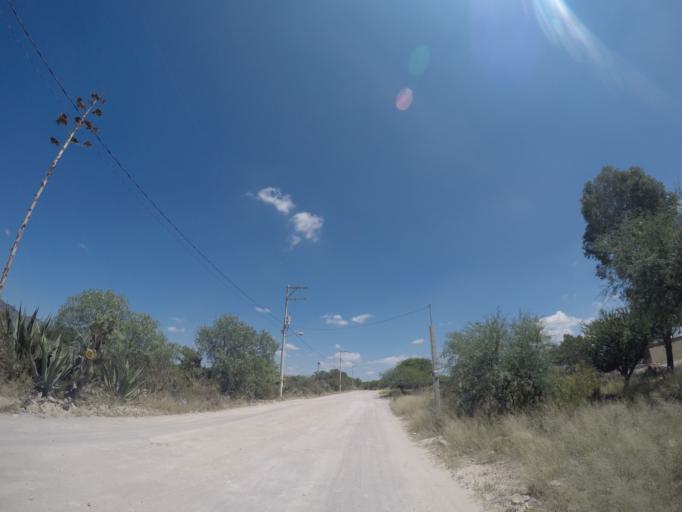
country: MX
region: San Luis Potosi
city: La Pila
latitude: 21.9966
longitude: -100.8987
